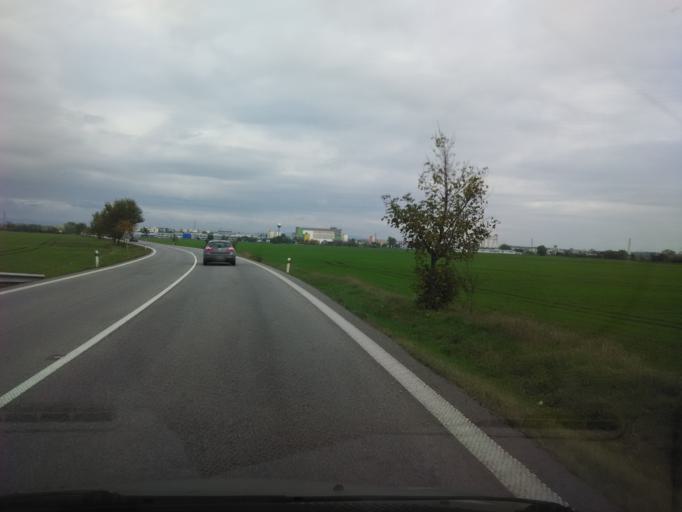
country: SK
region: Nitriansky
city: Levice
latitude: 48.2029
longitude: 18.5686
